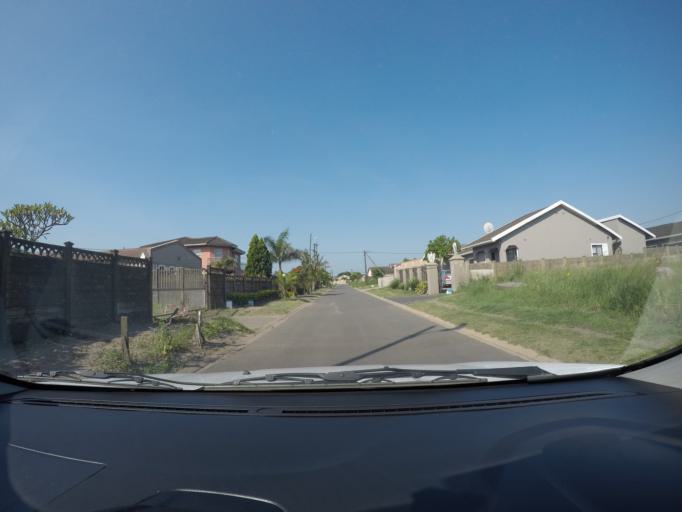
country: ZA
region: KwaZulu-Natal
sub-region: uThungulu District Municipality
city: Richards Bay
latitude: -28.7212
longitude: 32.0365
